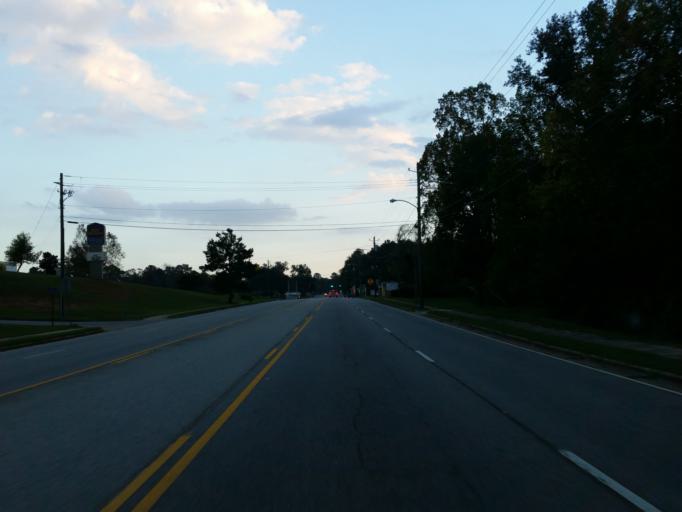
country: US
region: Georgia
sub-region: Pulaski County
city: Hawkinsville
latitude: 32.2879
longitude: -83.4810
